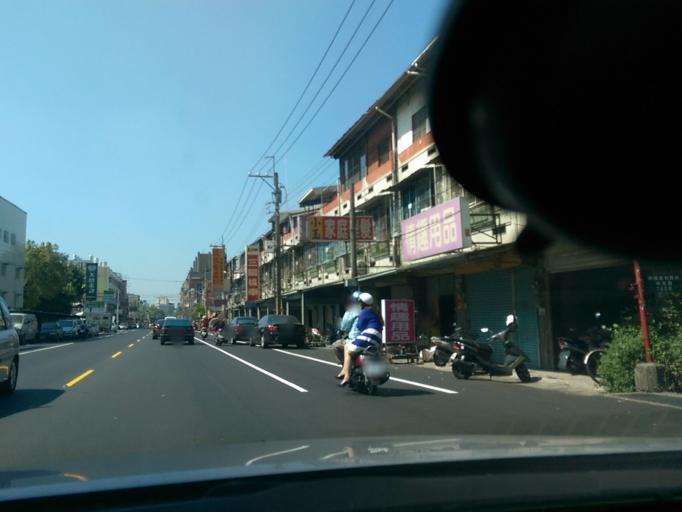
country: TW
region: Taiwan
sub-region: Chiayi
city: Jiayi Shi
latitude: 23.4472
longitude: 120.4581
